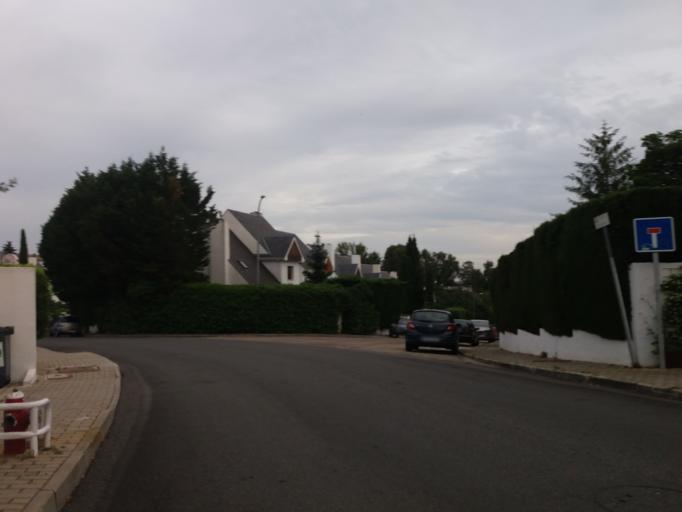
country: ES
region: Madrid
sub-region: Provincia de Madrid
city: Galapagar
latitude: 40.5942
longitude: -3.9727
